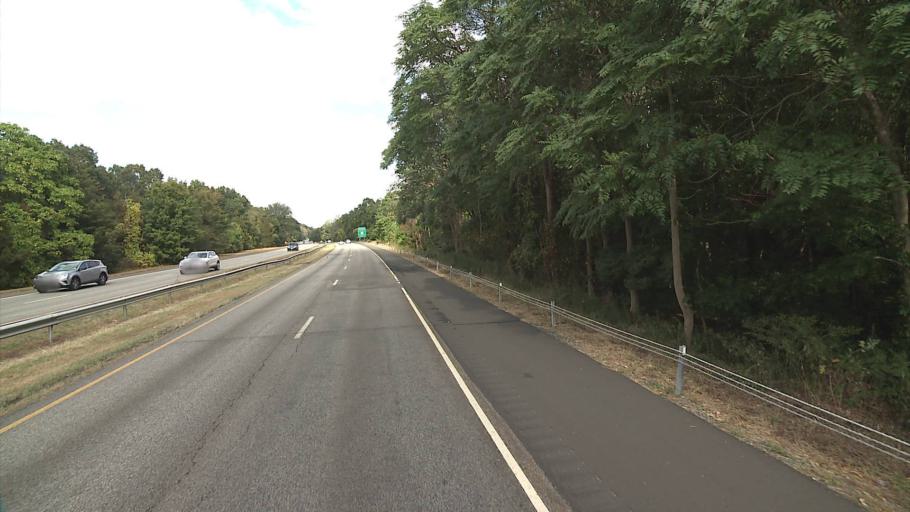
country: US
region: Connecticut
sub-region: New Haven County
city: Wallingford
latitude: 41.4460
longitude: -72.8435
